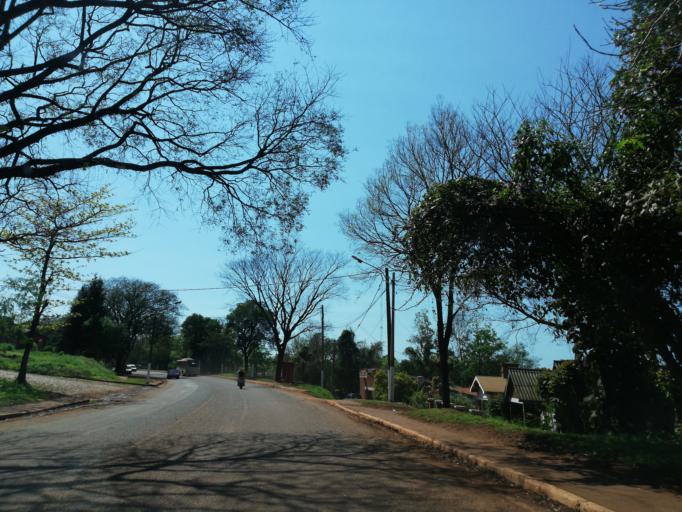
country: AR
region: Misiones
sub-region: Departamento de Eldorado
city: Eldorado
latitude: -26.4089
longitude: -54.6433
